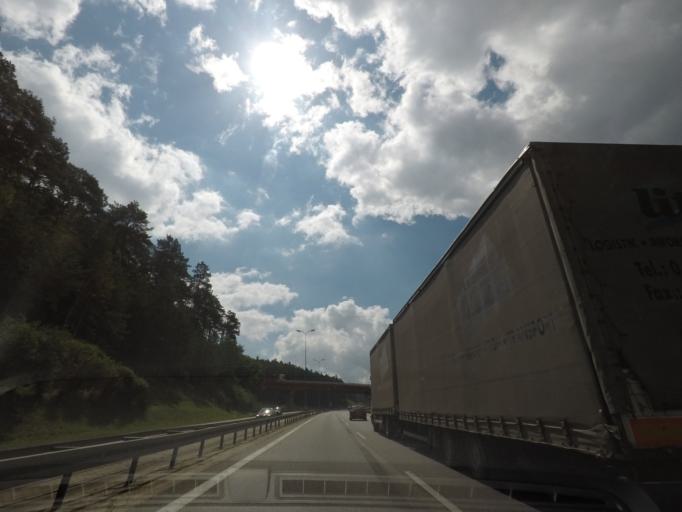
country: PL
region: Pomeranian Voivodeship
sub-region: Gdynia
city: Pogorze
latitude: 54.5193
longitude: 18.4576
